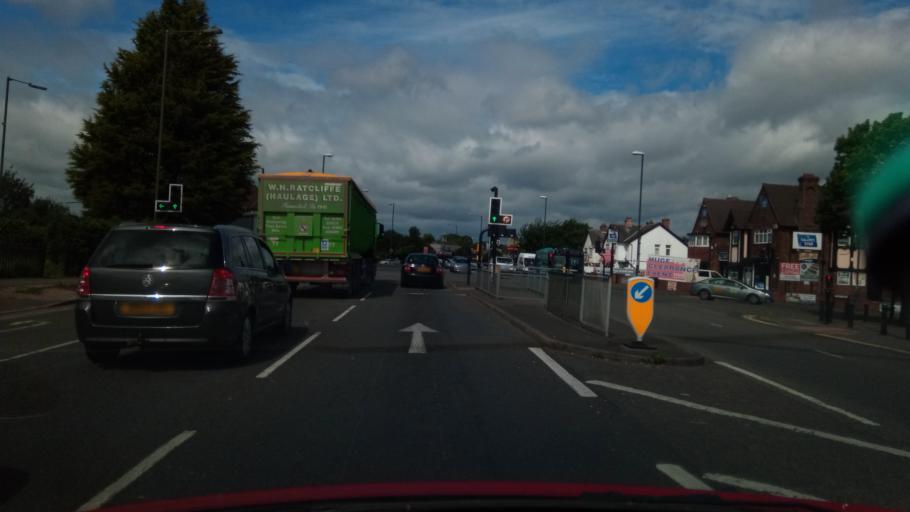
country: GB
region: England
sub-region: Derby
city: Derby
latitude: 52.8963
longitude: -1.4693
